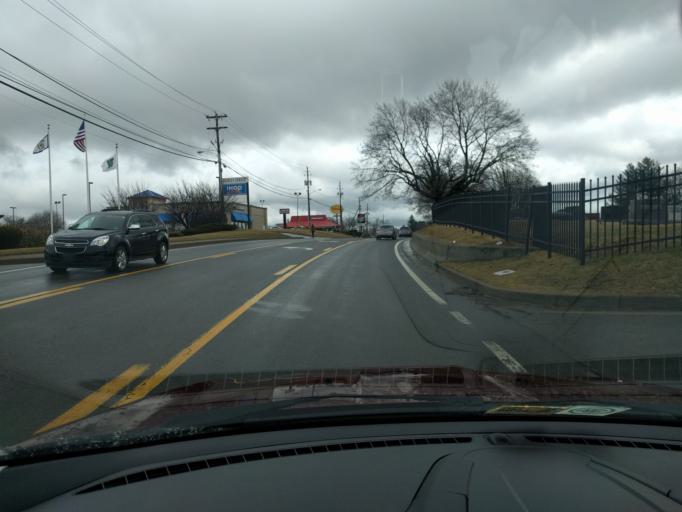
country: US
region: West Virginia
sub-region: Raleigh County
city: Mabscott
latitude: 37.7910
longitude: -81.2125
